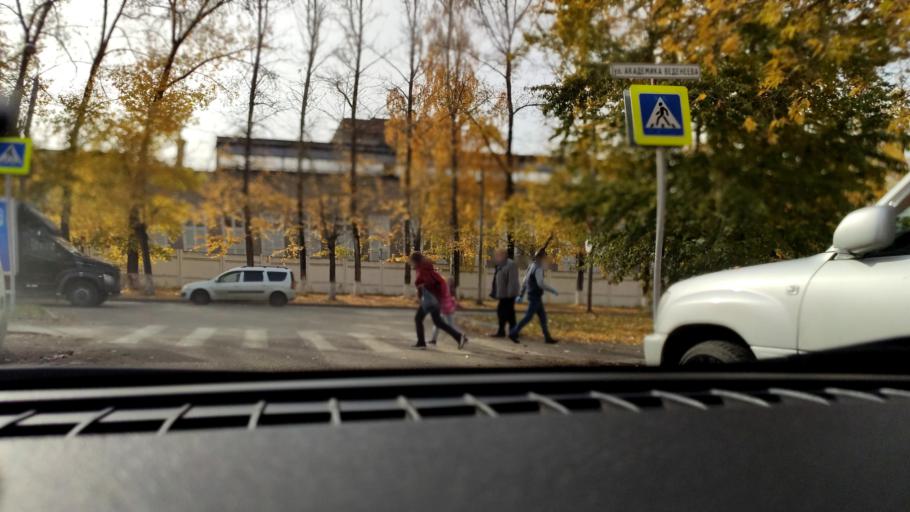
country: RU
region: Perm
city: Perm
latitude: 58.1100
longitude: 56.3756
